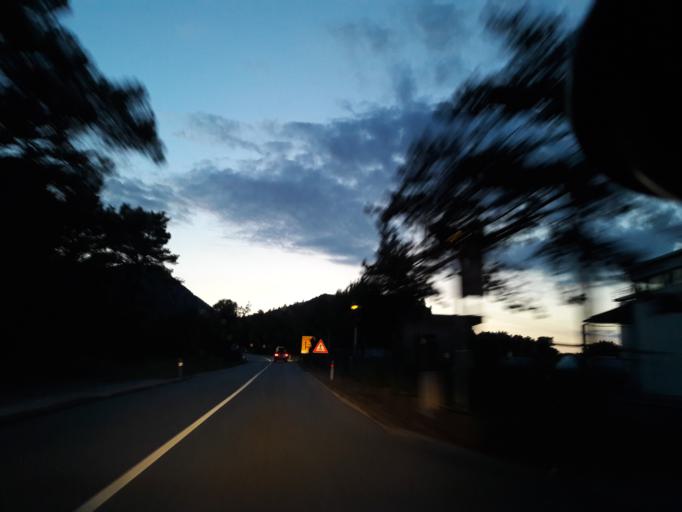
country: HR
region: Dubrovacko-Neretvanska
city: Orebic
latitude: 42.9697
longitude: 17.2990
